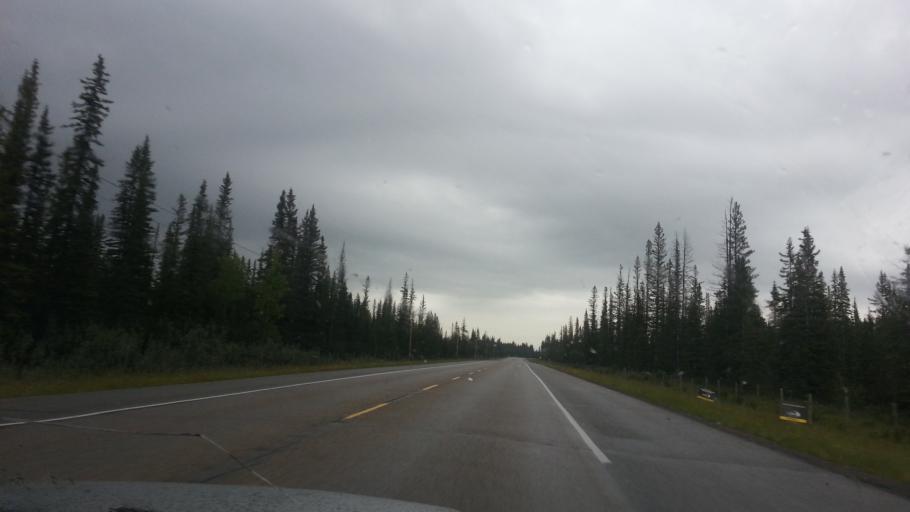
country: CA
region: Alberta
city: Cochrane
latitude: 50.9668
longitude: -114.5417
